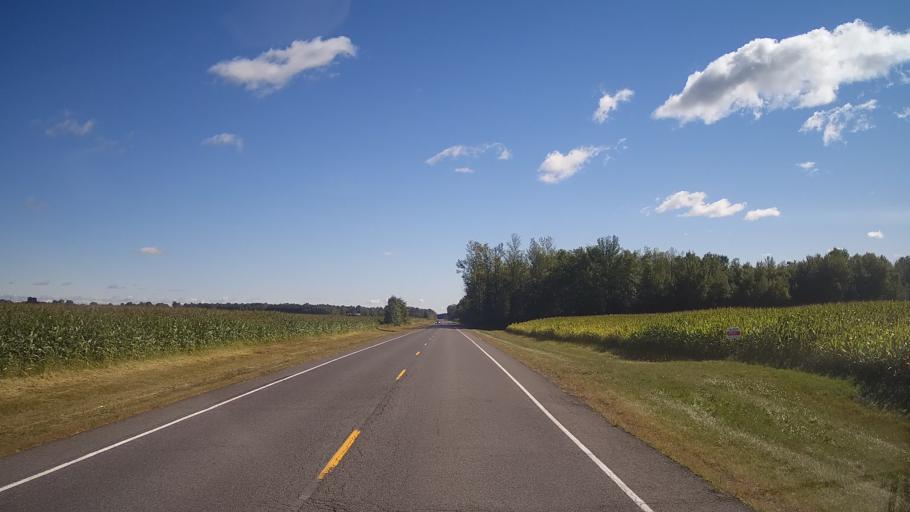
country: CA
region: Ontario
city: Prescott
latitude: 44.9071
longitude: -75.4364
